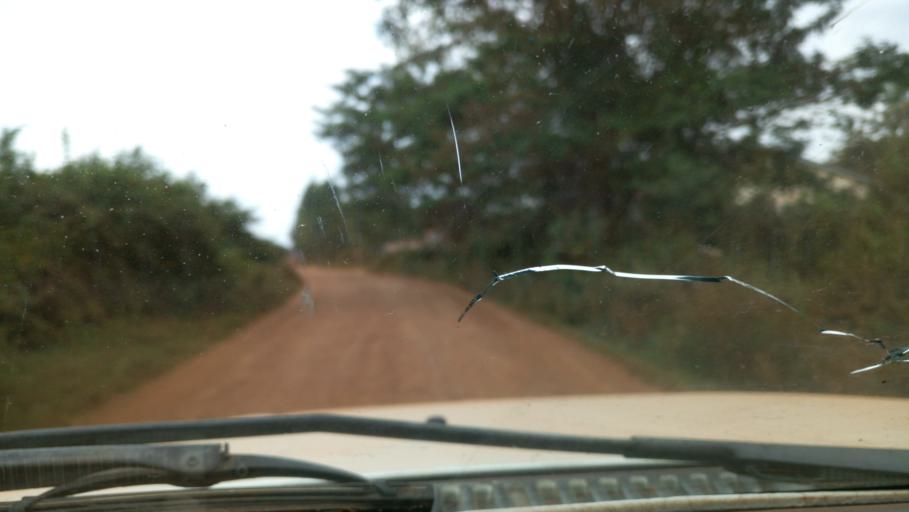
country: KE
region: Murang'a District
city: Maragua
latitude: -0.7897
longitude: 37.1256
